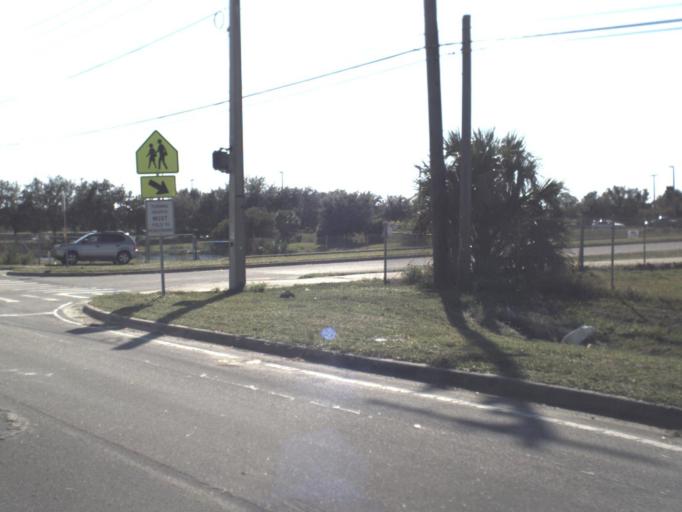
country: US
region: Florida
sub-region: Brevard County
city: South Patrick Shores
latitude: 28.1784
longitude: -80.6721
